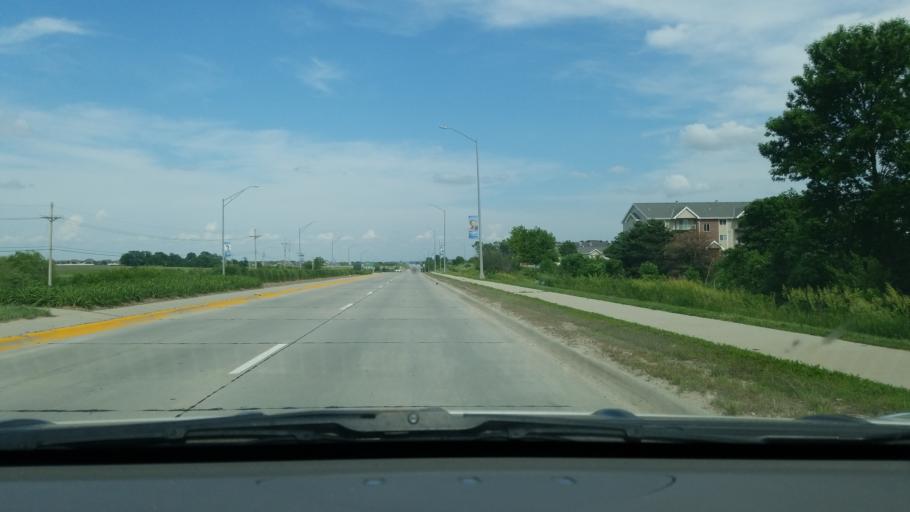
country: US
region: Nebraska
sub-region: Sarpy County
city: Gretna
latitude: 41.1469
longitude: -96.2322
